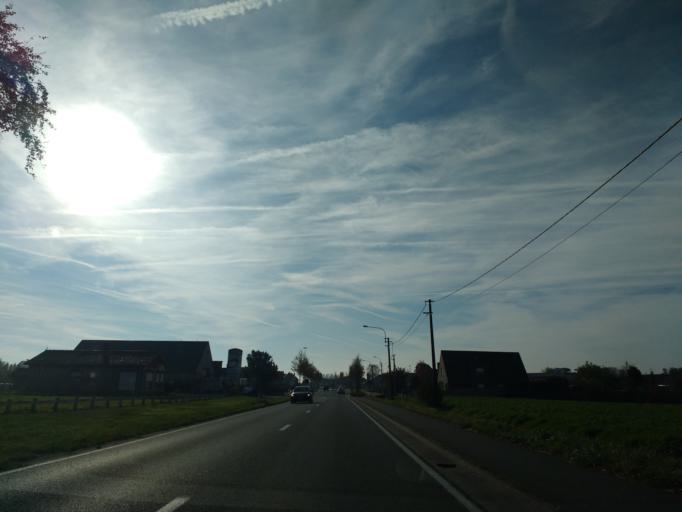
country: BE
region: Flanders
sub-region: Provincie Oost-Vlaanderen
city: Kaprijke
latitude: 51.2513
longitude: 3.6130
